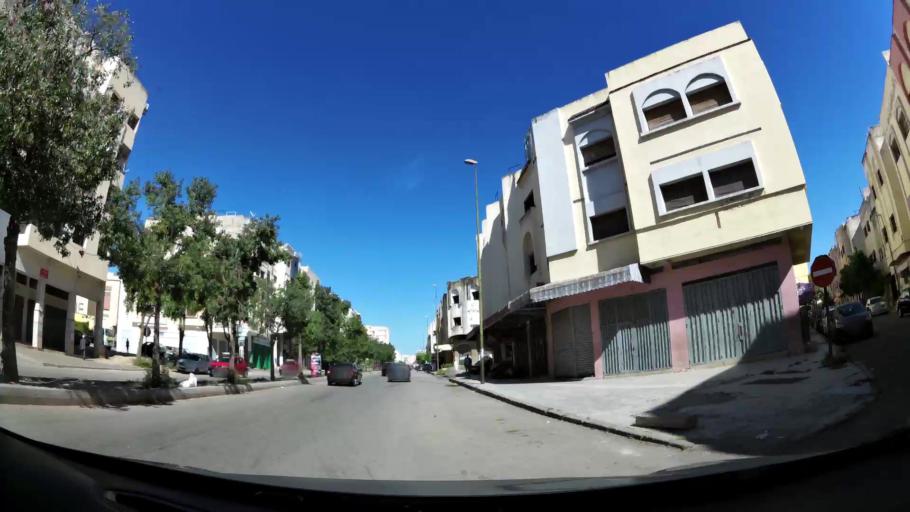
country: MA
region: Fes-Boulemane
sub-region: Fes
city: Fes
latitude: 34.0135
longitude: -4.9815
